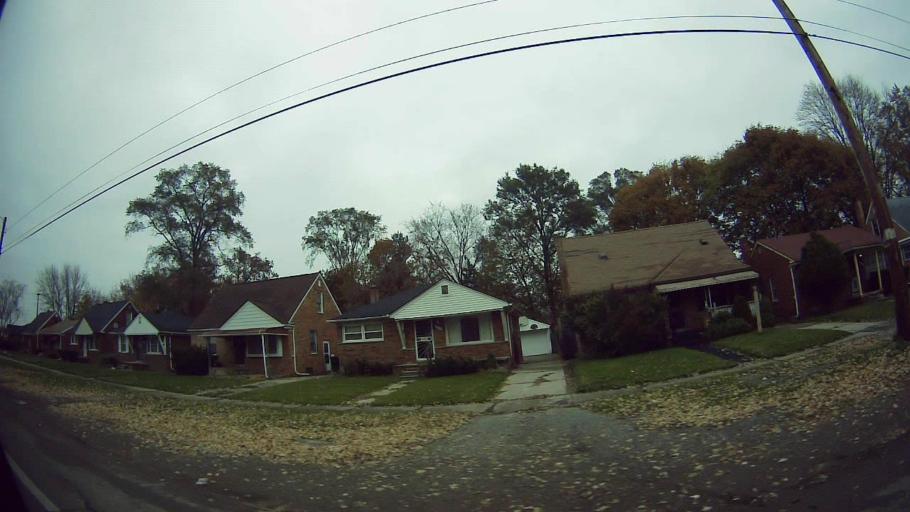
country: US
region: Michigan
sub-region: Oakland County
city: Southfield
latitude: 42.4408
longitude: -83.2587
